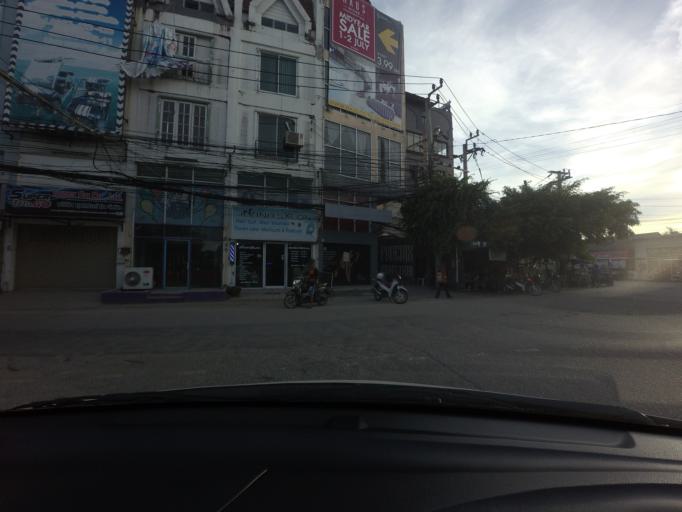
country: TH
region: Nonthaburi
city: Mueang Nonthaburi
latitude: 13.8880
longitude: 100.5236
